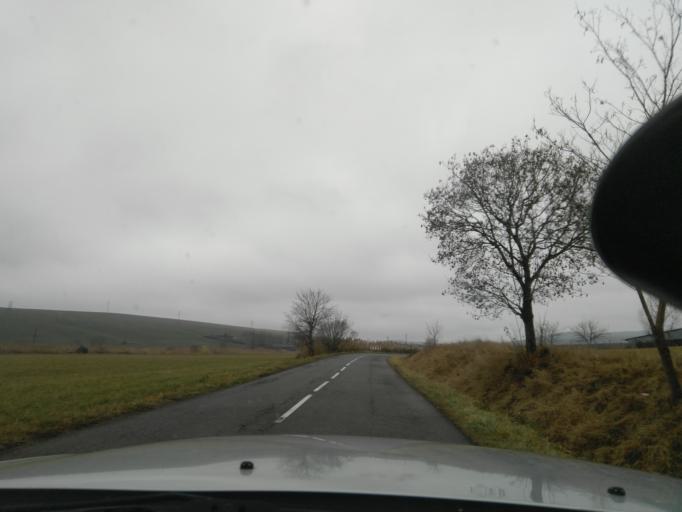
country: HU
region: Nograd
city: Kazar
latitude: 48.0411
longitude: 19.8737
